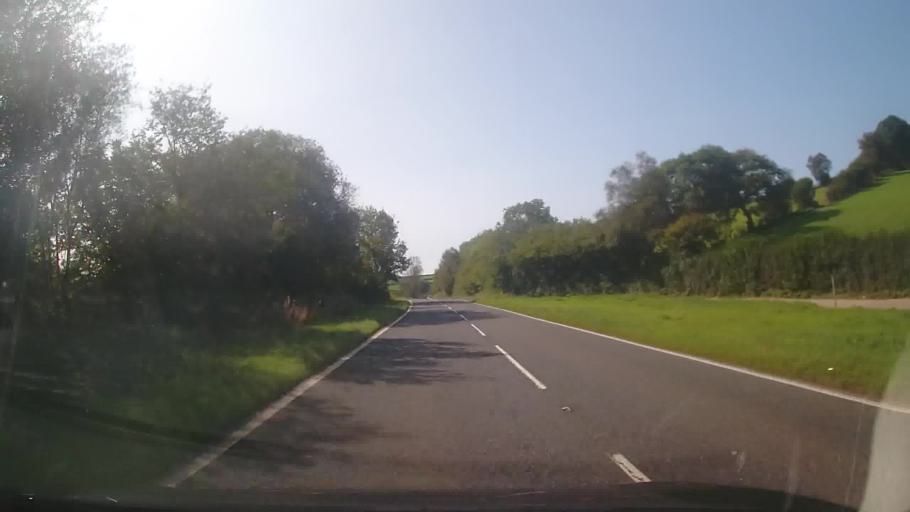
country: GB
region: Wales
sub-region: Sir Powys
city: Rhayader
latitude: 52.1445
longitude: -3.5908
